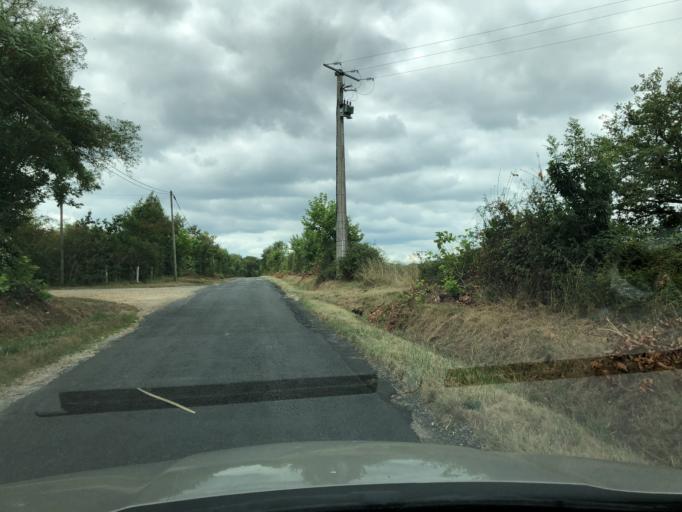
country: FR
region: Centre
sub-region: Departement d'Indre-et-Loire
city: Mazieres-de-Touraine
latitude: 47.3875
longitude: 0.4418
